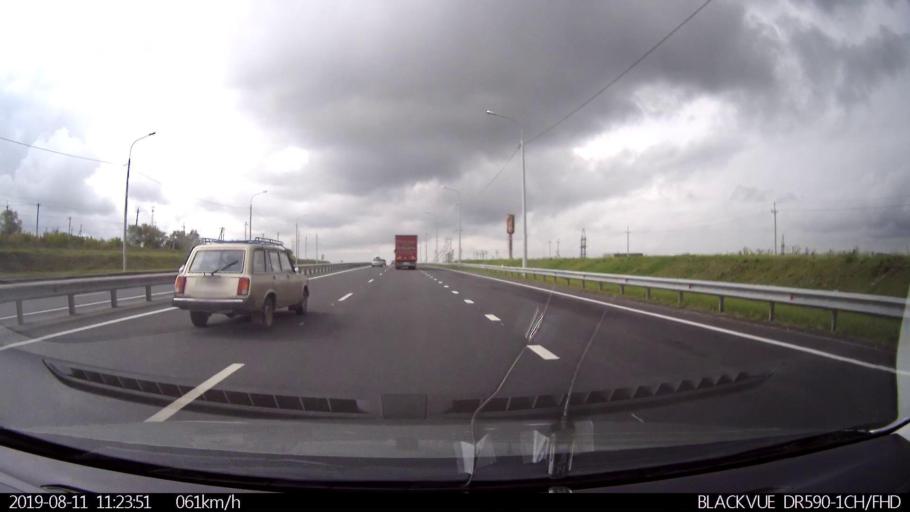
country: RU
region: Ulyanovsk
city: Krasnyy Gulyay
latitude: 54.1324
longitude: 48.2484
